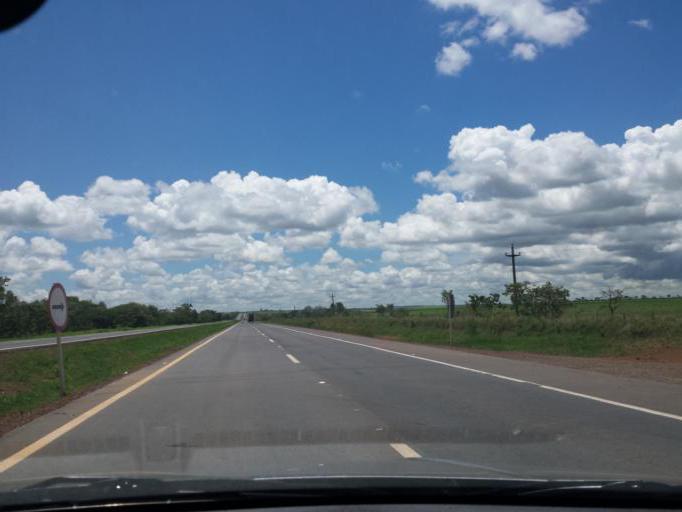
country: BR
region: Goias
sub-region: Cristalina
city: Cristalina
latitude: -16.6777
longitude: -47.7077
